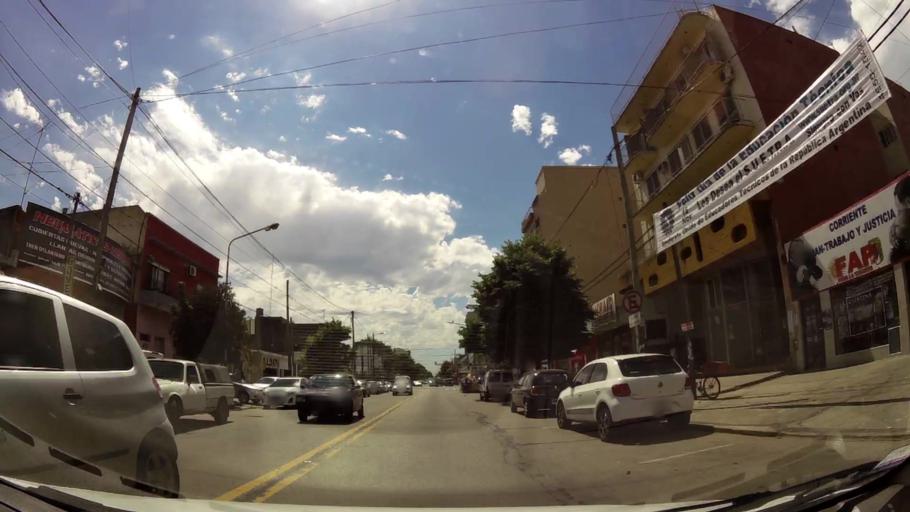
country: AR
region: Buenos Aires
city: San Justo
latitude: -34.6736
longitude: -58.5605
